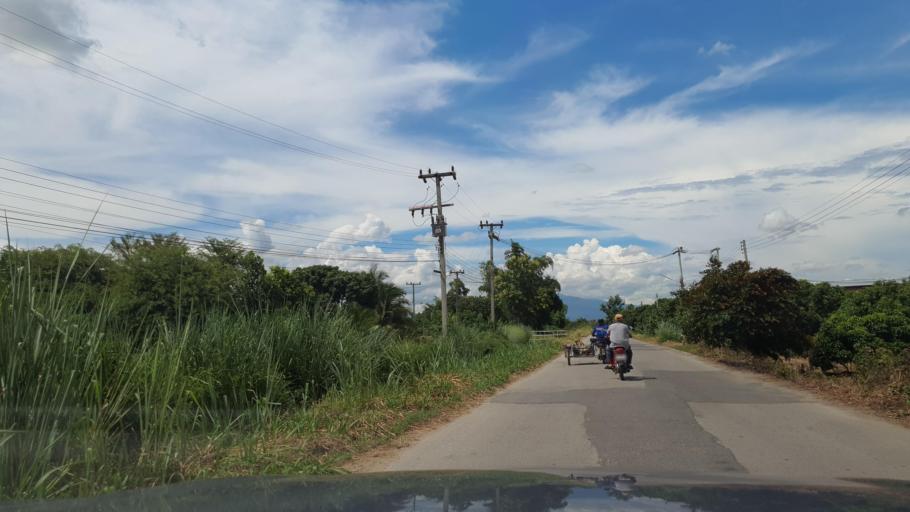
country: TH
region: Chiang Mai
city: San Pa Tong
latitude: 18.5843
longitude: 98.9061
